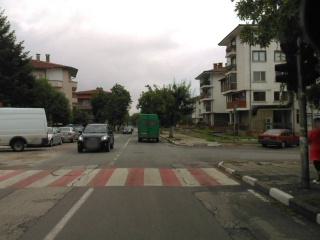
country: BG
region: Plovdiv
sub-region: Obshtina Karlovo
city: Karlovo
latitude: 42.6527
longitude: 24.7587
